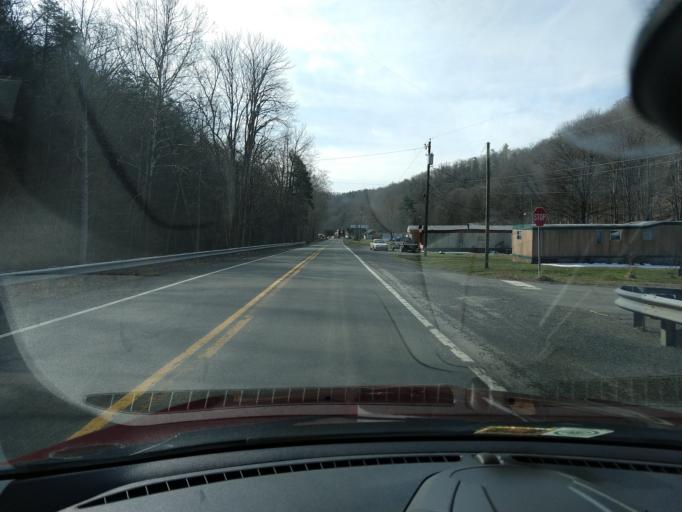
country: US
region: West Virginia
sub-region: Pocahontas County
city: Marlinton
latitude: 38.1942
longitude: -80.1358
